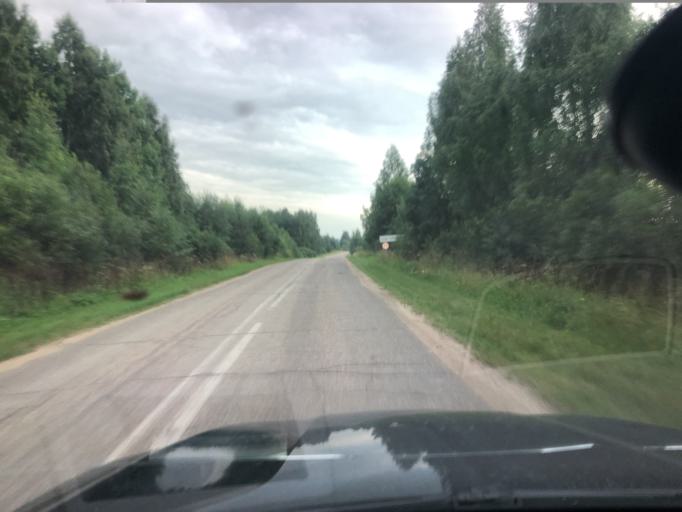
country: RU
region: Jaroslavl
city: Pereslavl'-Zalesskiy
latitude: 57.0120
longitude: 38.9685
